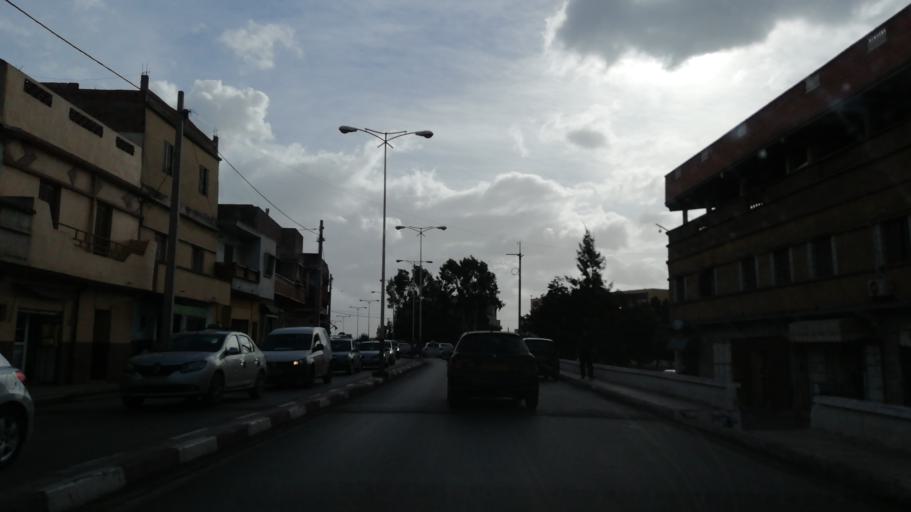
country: DZ
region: Oran
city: Oran
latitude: 35.6857
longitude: -0.6208
